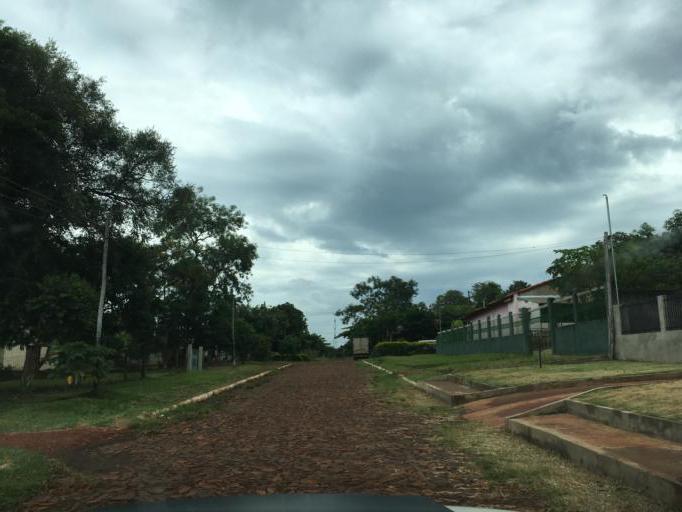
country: PY
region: Alto Parana
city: Ciudad del Este
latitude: -25.4133
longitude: -54.6533
